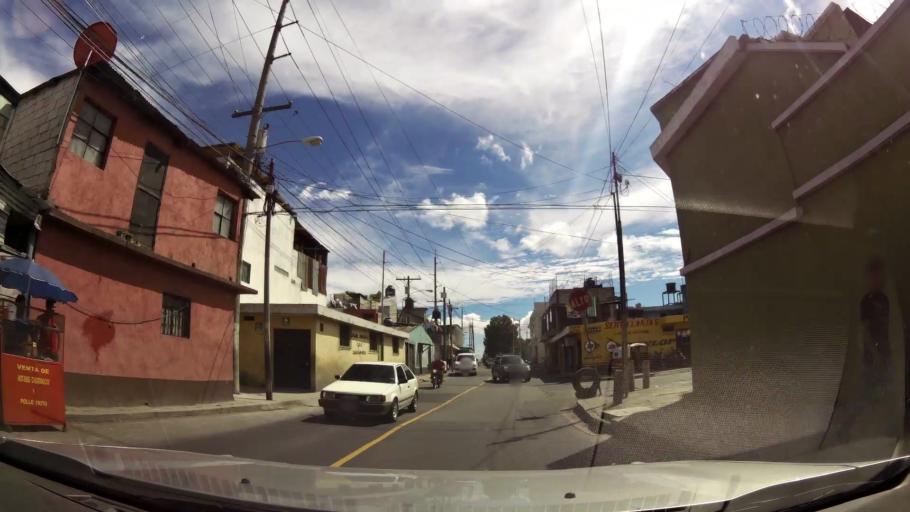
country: GT
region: Guatemala
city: Mixco
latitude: 14.6593
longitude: -90.5706
